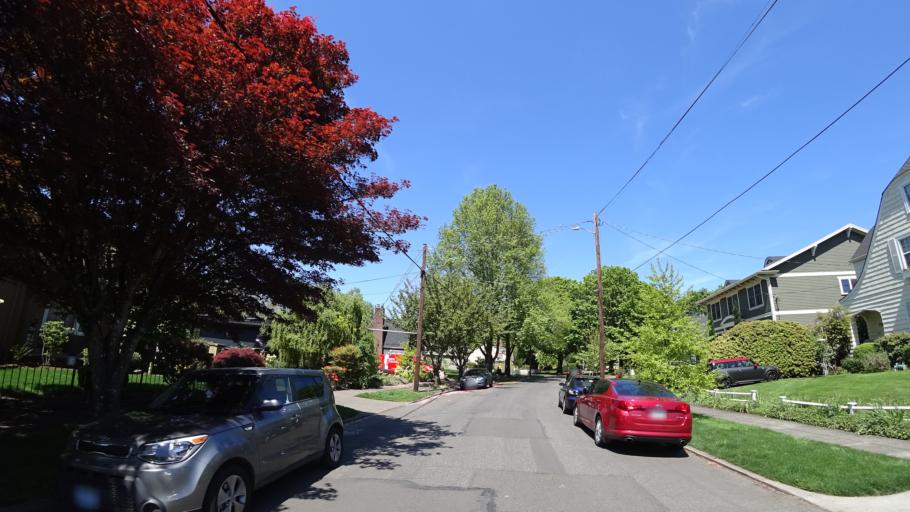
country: US
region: Oregon
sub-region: Clackamas County
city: Milwaukie
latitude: 45.4725
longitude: -122.6347
